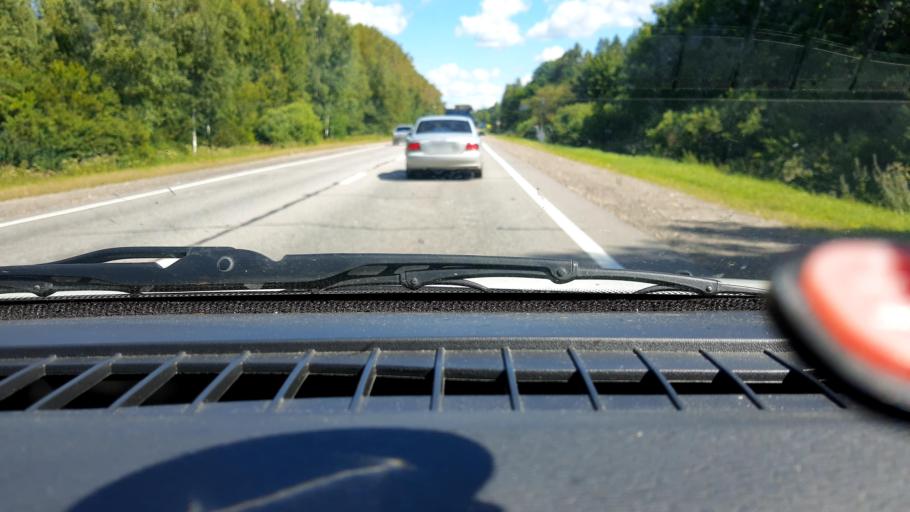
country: RU
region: Nizjnij Novgorod
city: Chernukha
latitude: 55.5643
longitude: 43.9560
